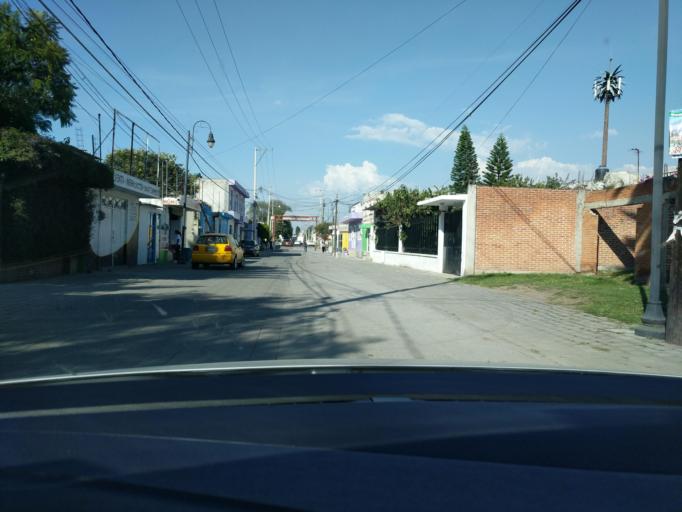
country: MX
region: Puebla
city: San Andres Cholula
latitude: 19.0315
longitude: -98.3192
